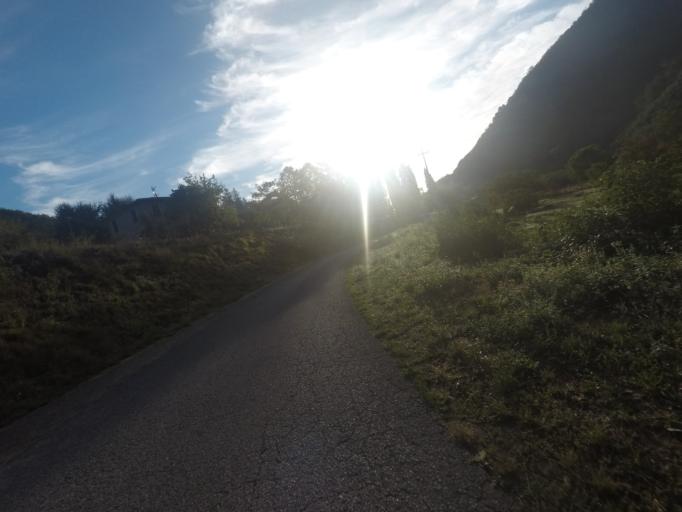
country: IT
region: Tuscany
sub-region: Provincia di Lucca
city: Pescaglia
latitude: 43.9524
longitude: 10.4218
